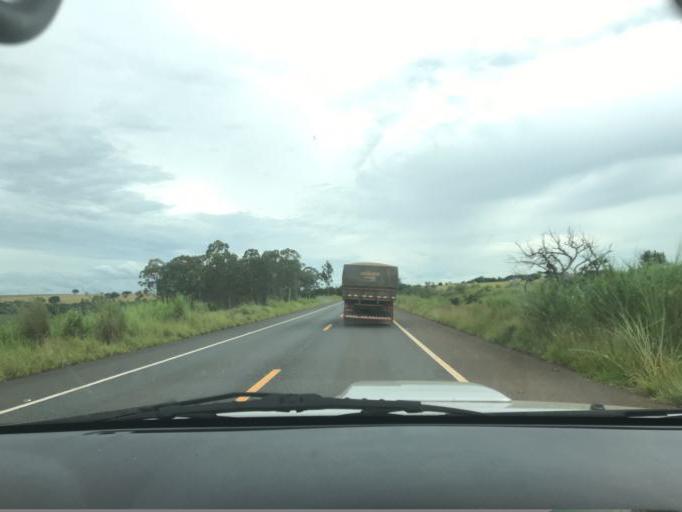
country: BR
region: Minas Gerais
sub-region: Araxa
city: Araxa
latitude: -19.3742
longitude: -46.8571
